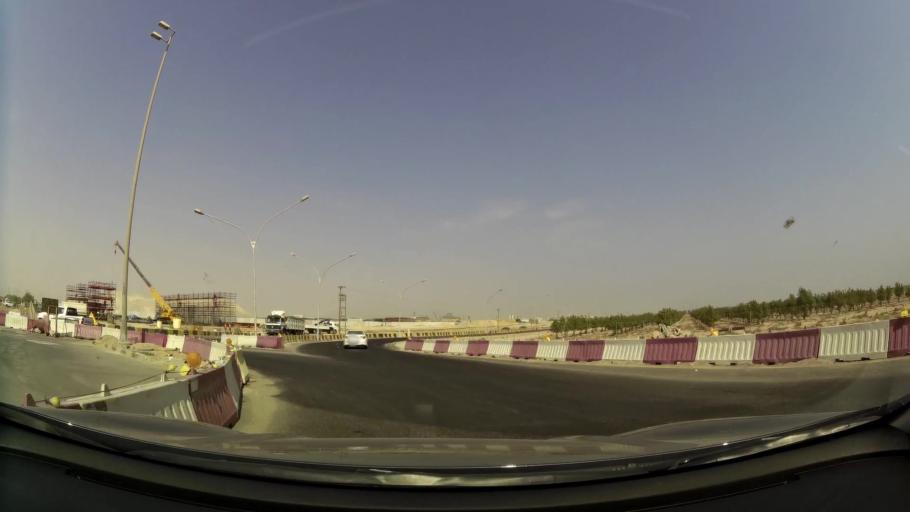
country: KW
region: Al Ahmadi
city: Al Fahahil
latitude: 28.9719
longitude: 48.1291
